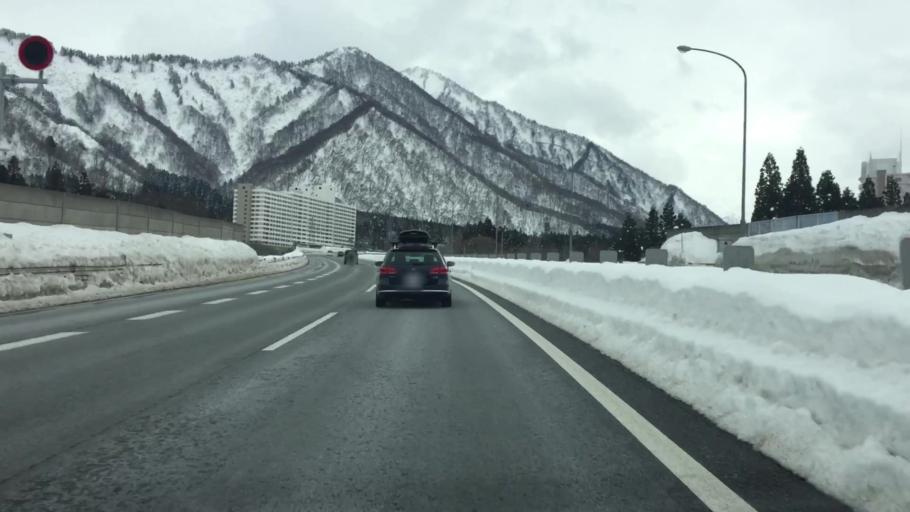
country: JP
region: Niigata
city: Shiozawa
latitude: 36.9080
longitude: 138.8425
